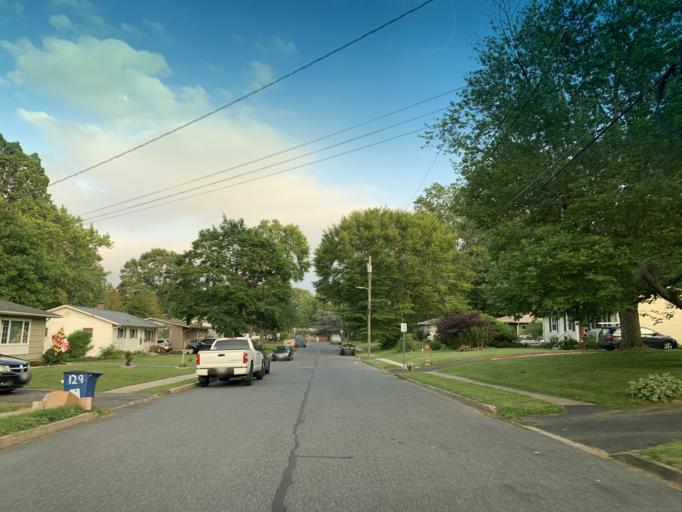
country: US
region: Maryland
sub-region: Harford County
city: Bel Air
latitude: 39.5409
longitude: -76.3470
